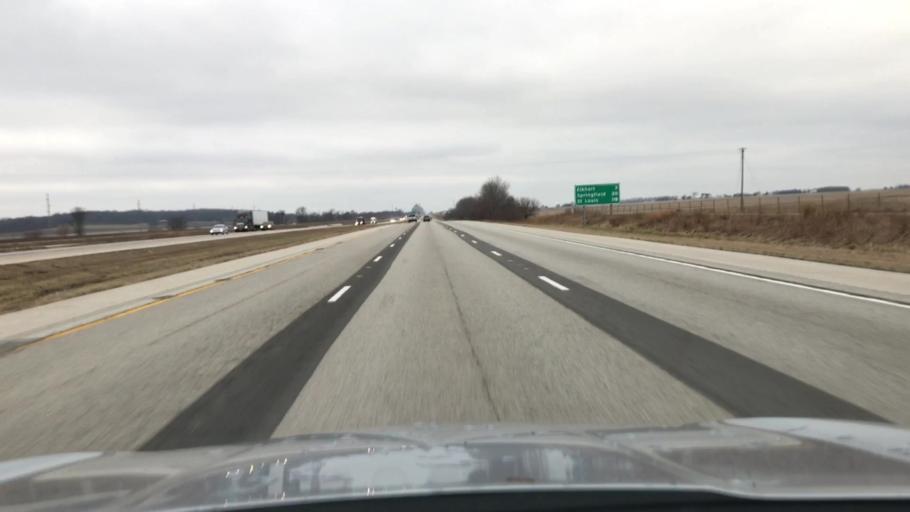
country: US
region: Illinois
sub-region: Sangamon County
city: Williamsville
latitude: 40.0503
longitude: -89.4591
